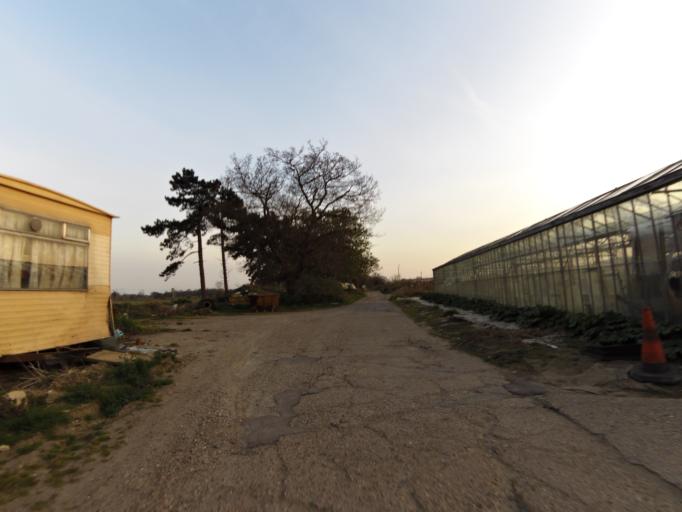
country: GB
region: England
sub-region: Suffolk
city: Kesgrave
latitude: 52.0265
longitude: 1.2290
